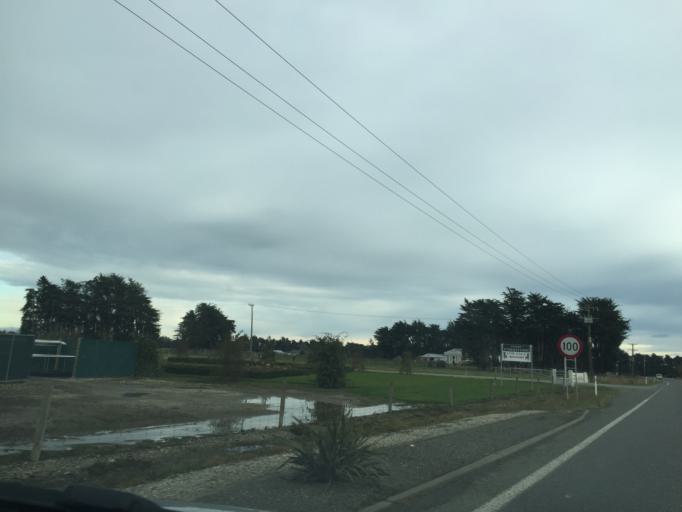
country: NZ
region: Southland
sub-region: Gore District
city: Gore
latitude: -46.3103
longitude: 168.7751
